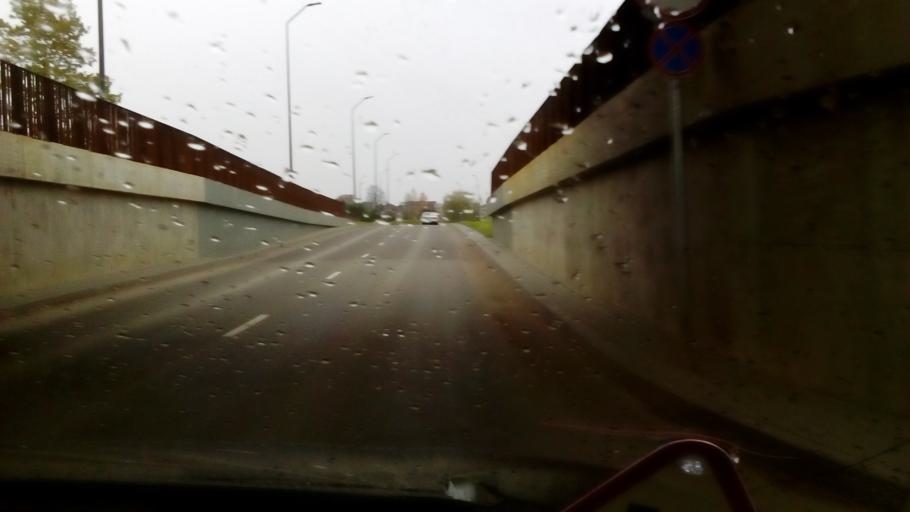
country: LT
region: Marijampoles apskritis
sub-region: Marijampole Municipality
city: Marijampole
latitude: 54.5444
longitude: 23.3556
